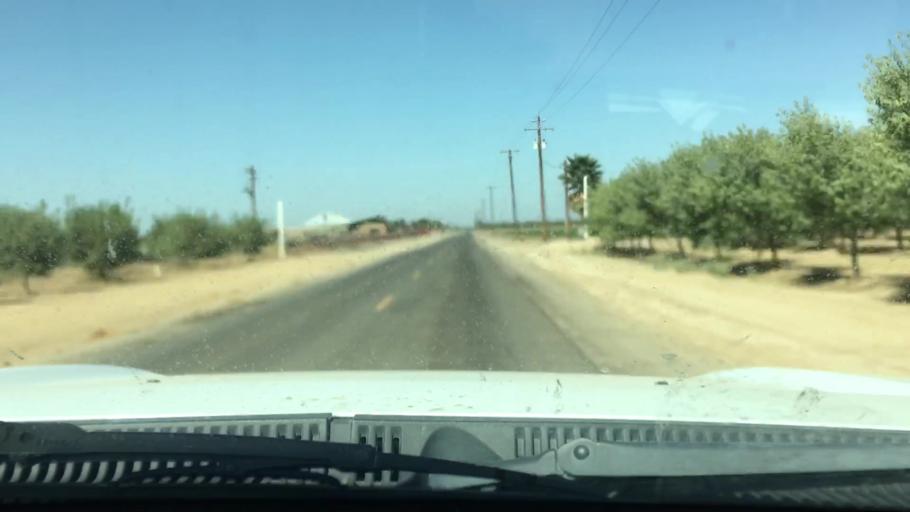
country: US
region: California
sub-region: Kern County
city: Shafter
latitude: 35.4662
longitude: -119.3143
